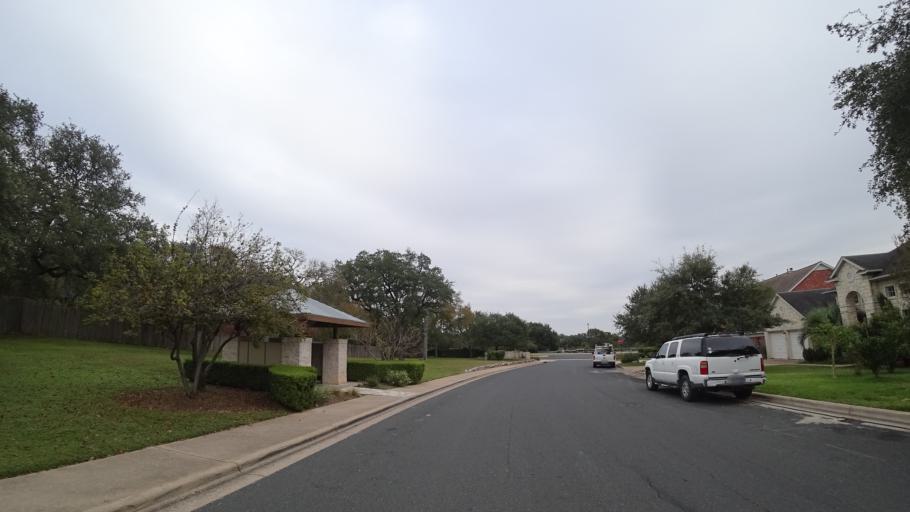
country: US
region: Texas
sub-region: Travis County
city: Shady Hollow
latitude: 30.1851
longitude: -97.8968
